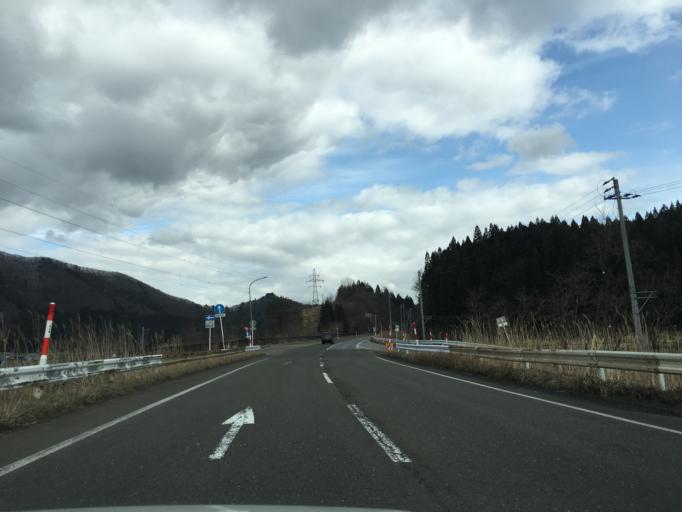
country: JP
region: Akita
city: Odate
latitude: 40.2218
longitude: 140.6527
